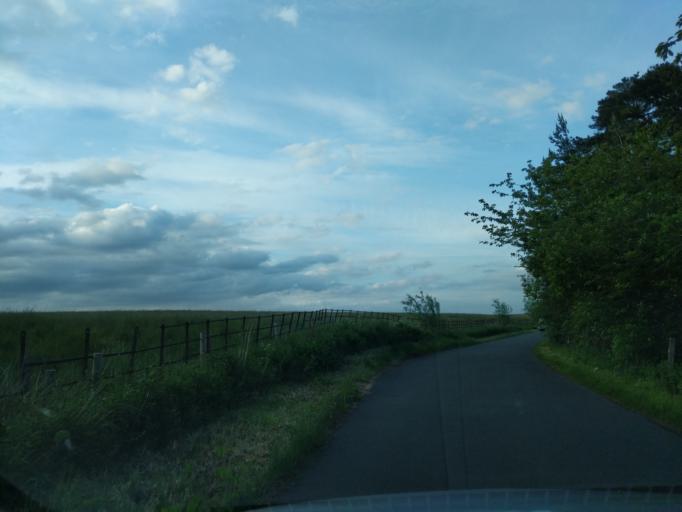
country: GB
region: Scotland
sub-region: Midlothian
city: Bonnyrigg
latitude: 55.7737
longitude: -3.1285
